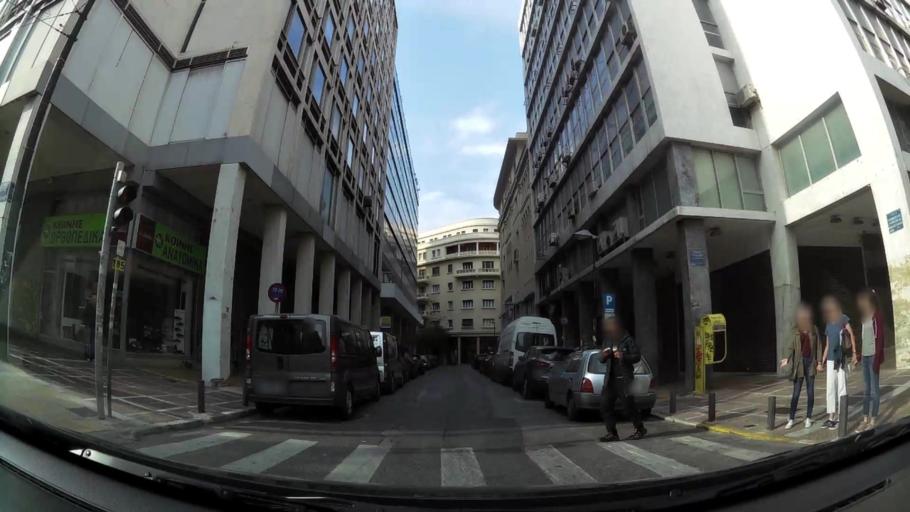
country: GR
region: Attica
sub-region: Nomarchia Athinas
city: Athens
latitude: 37.9808
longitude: 23.7308
